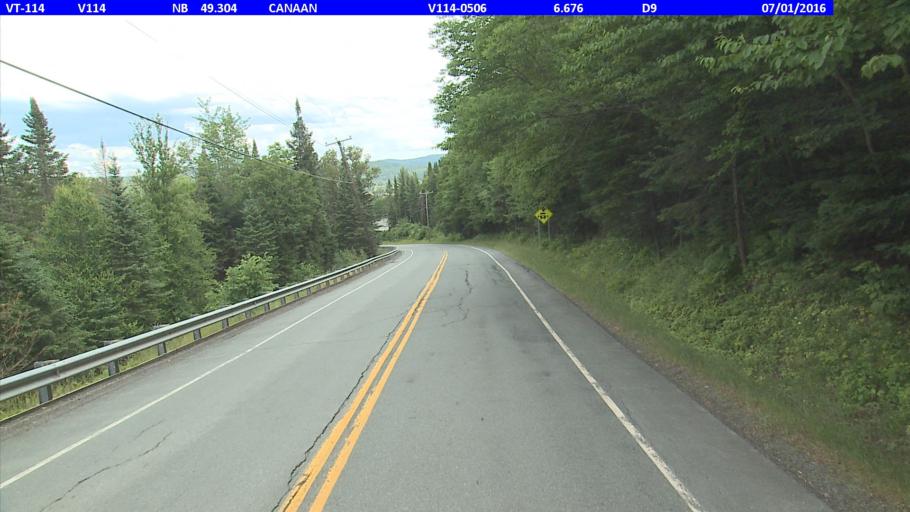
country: US
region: New Hampshire
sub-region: Coos County
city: Colebrook
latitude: 45.0088
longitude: -71.5625
